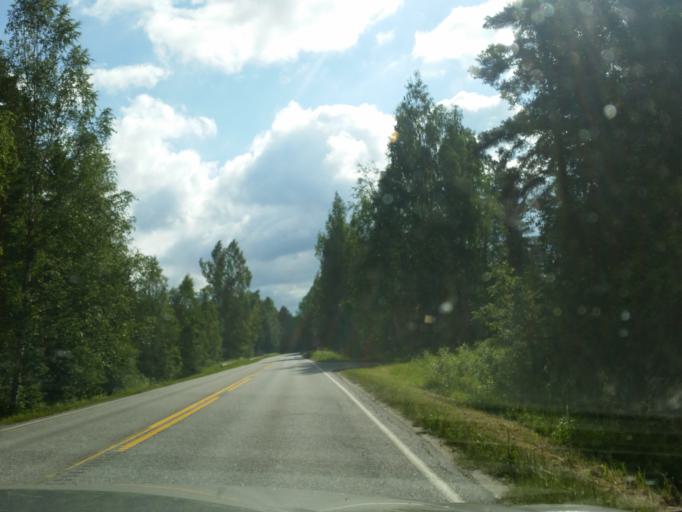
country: FI
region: Northern Savo
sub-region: Kuopio
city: Karttula
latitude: 62.8948
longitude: 27.0139
